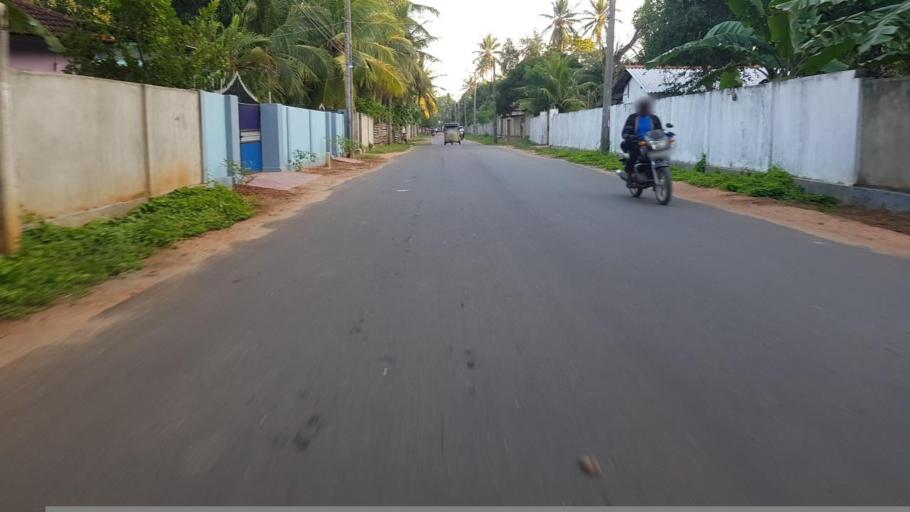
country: LK
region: Northern Province
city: Jaffna
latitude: 9.7146
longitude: 79.9851
